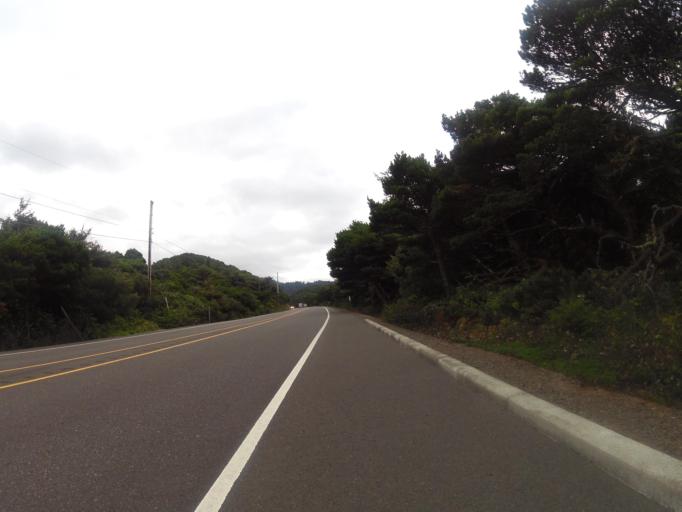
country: US
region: Oregon
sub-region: Lane County
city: Florence
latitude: 44.1585
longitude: -124.1157
